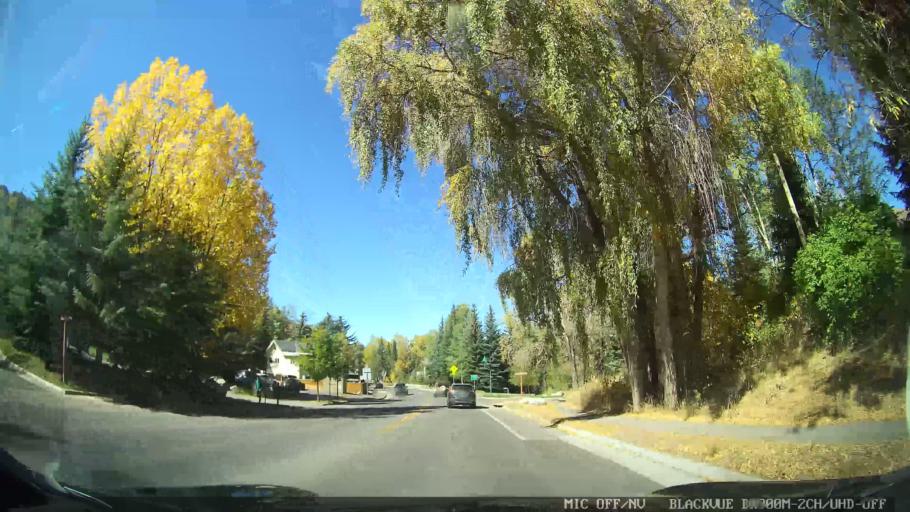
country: US
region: Colorado
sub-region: Pitkin County
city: Aspen
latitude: 39.1858
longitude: -106.8092
